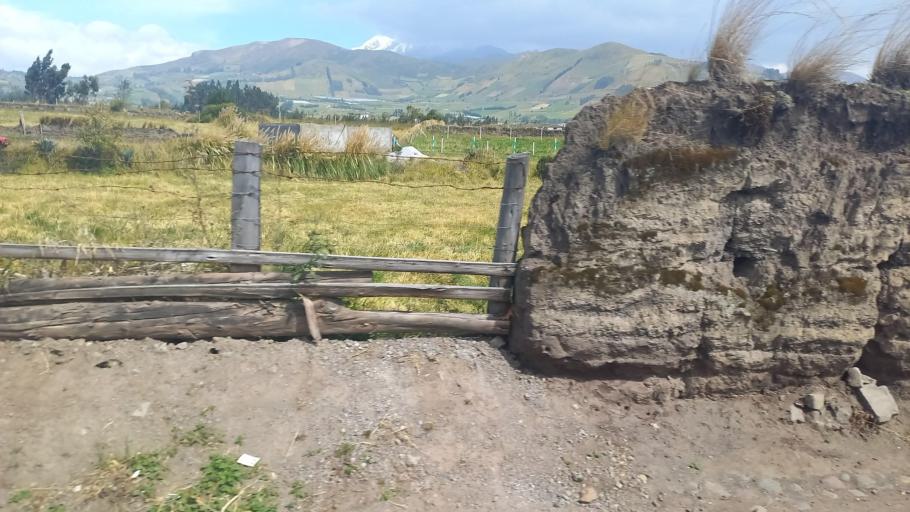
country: EC
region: Pichincha
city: Cayambe
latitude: 0.1416
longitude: -78.0732
